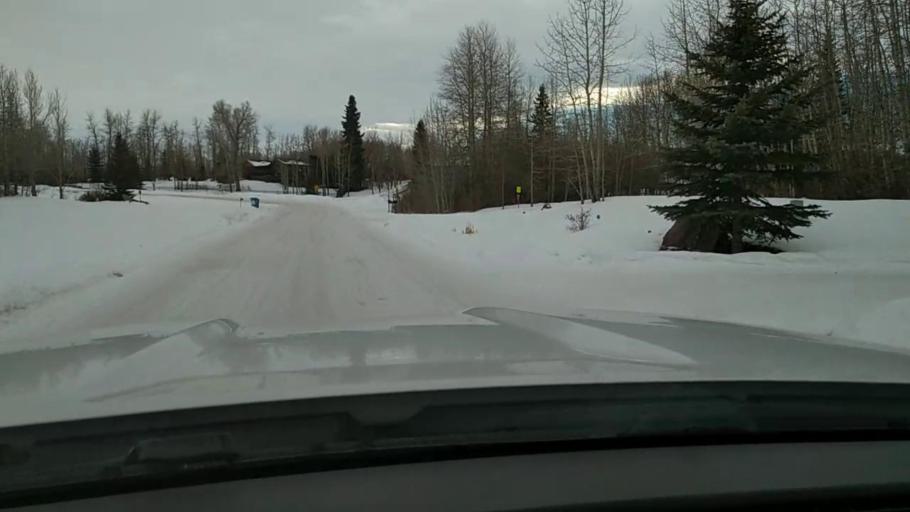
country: CA
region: Alberta
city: Cochrane
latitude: 51.1813
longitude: -114.2559
